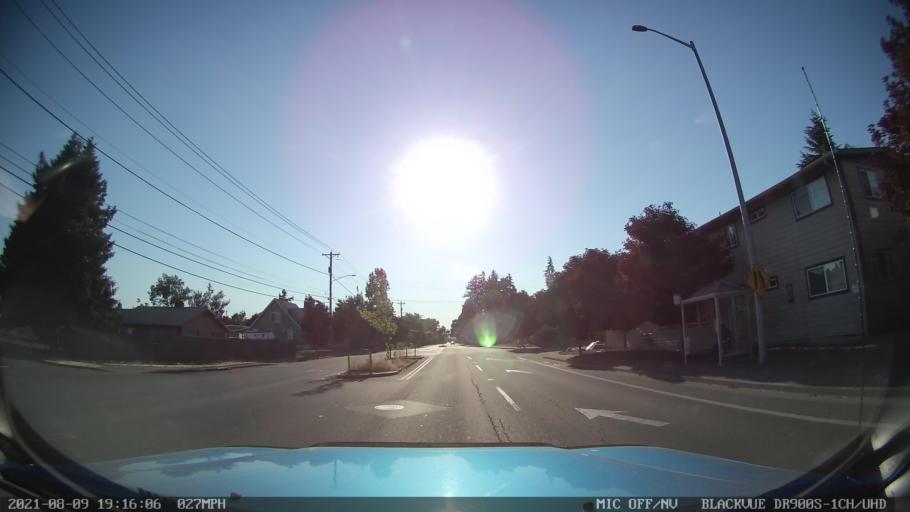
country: US
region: Oregon
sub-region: Marion County
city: Four Corners
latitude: 44.9399
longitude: -122.9928
